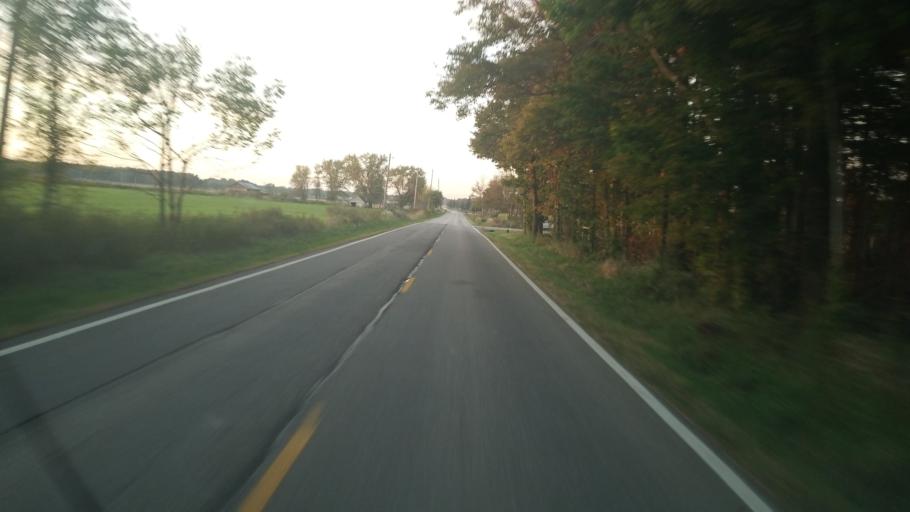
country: US
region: Ohio
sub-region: Ashtabula County
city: Andover
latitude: 41.6558
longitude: -80.6670
